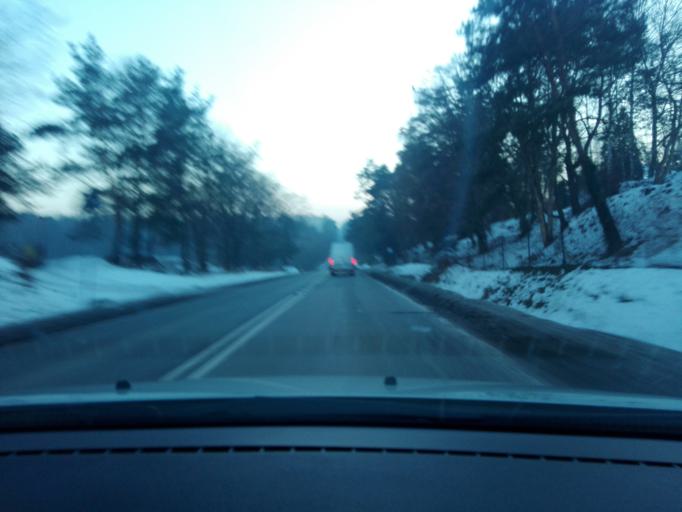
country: PL
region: Lodz Voivodeship
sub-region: Powiat zgierski
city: Zgierz
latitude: 51.8855
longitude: 19.4162
